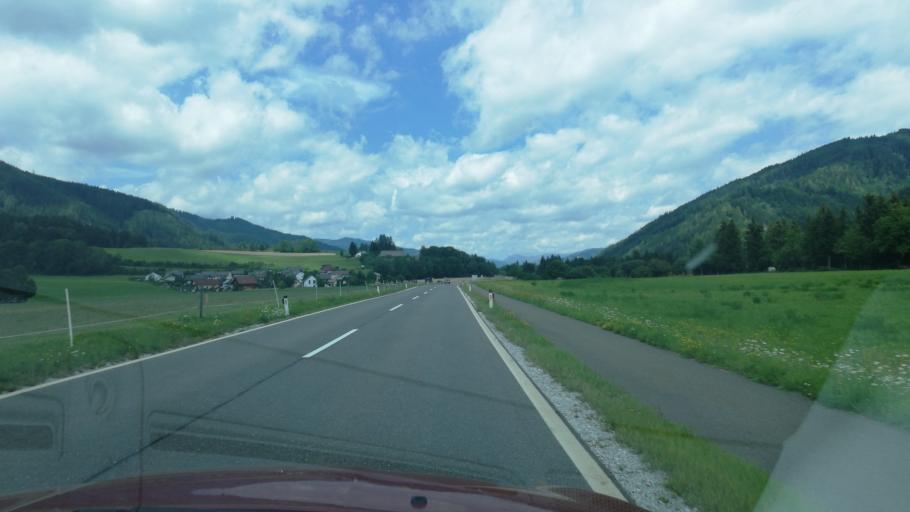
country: AT
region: Styria
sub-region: Politischer Bezirk Murtal
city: Oberkurzheim
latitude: 47.2297
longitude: 14.5533
